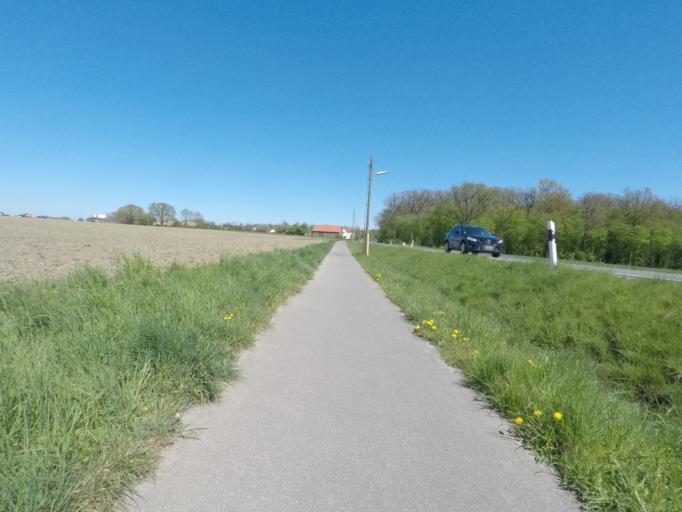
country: DE
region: North Rhine-Westphalia
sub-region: Regierungsbezirk Detmold
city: Leopoldshohe
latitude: 52.0379
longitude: 8.6405
